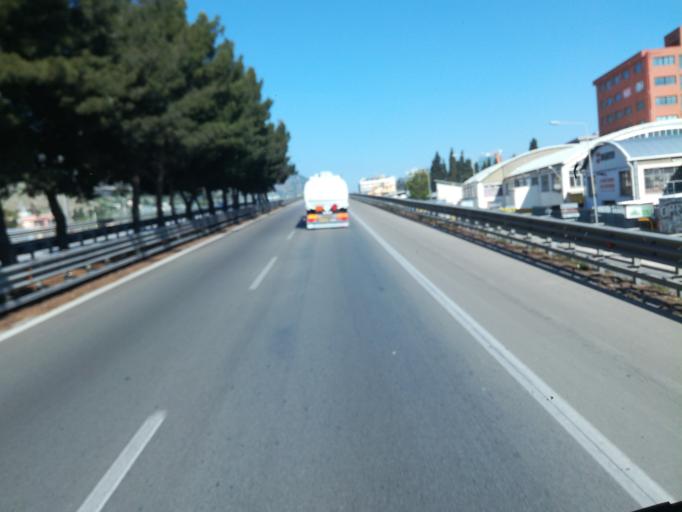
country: IT
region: Sicily
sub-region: Palermo
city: Palermo
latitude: 38.1542
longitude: 13.3195
